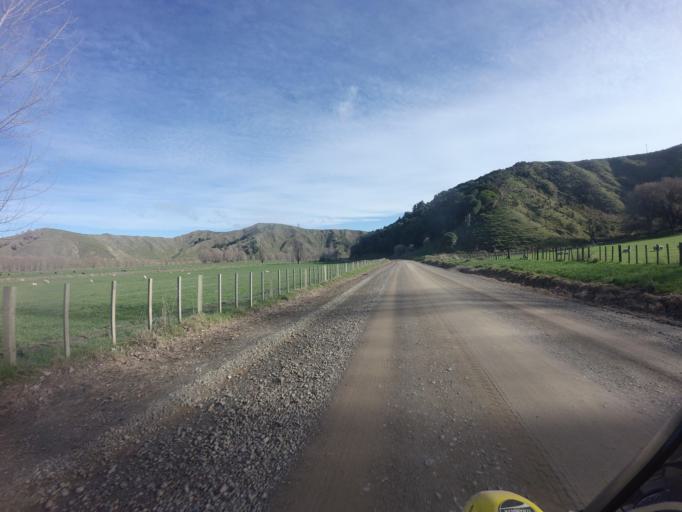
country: NZ
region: Hawke's Bay
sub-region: Wairoa District
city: Wairoa
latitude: -39.0251
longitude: 177.5755
